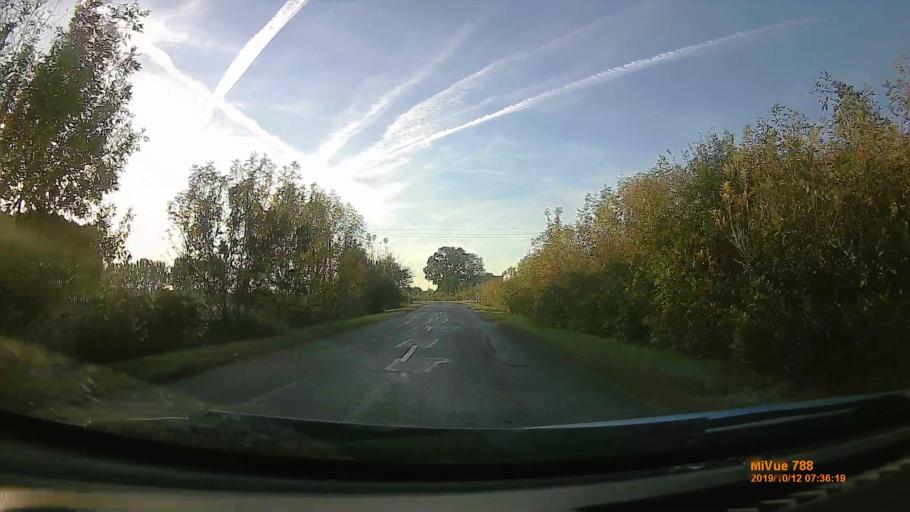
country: HU
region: Hajdu-Bihar
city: Pocsaj
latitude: 47.2461
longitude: 21.8131
